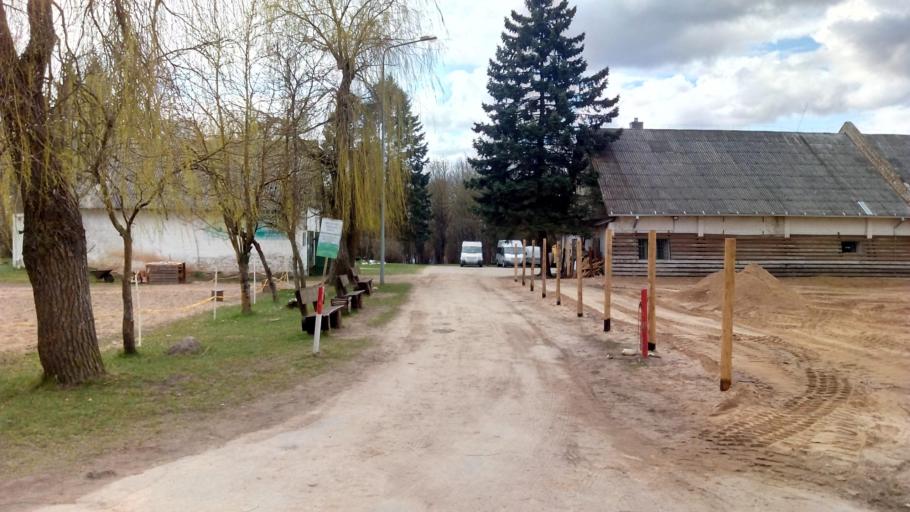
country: LT
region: Siauliu apskritis
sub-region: Siauliai
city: Siauliai
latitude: 55.9276
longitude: 23.3420
